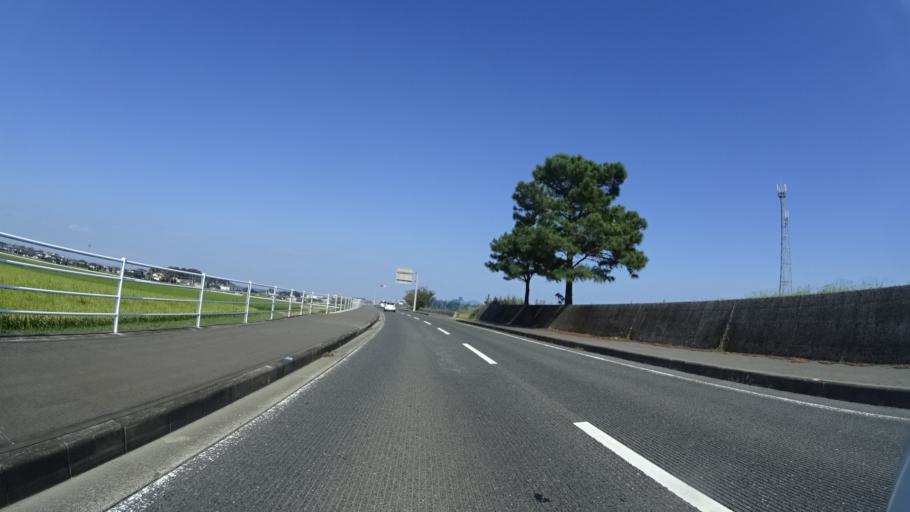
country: JP
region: Fukuoka
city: Shiida
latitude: 33.6448
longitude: 131.0626
